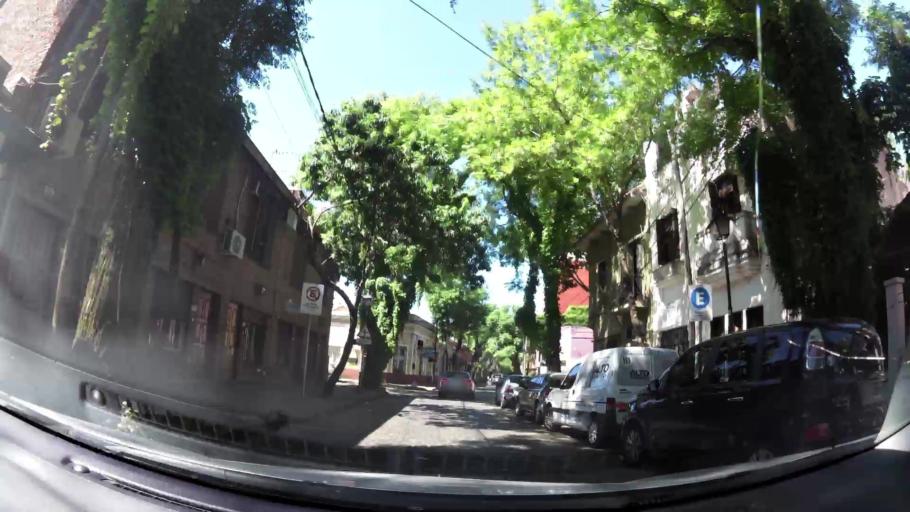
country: AR
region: Buenos Aires
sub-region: Partido de San Isidro
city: San Isidro
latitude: -34.4680
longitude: -58.5127
